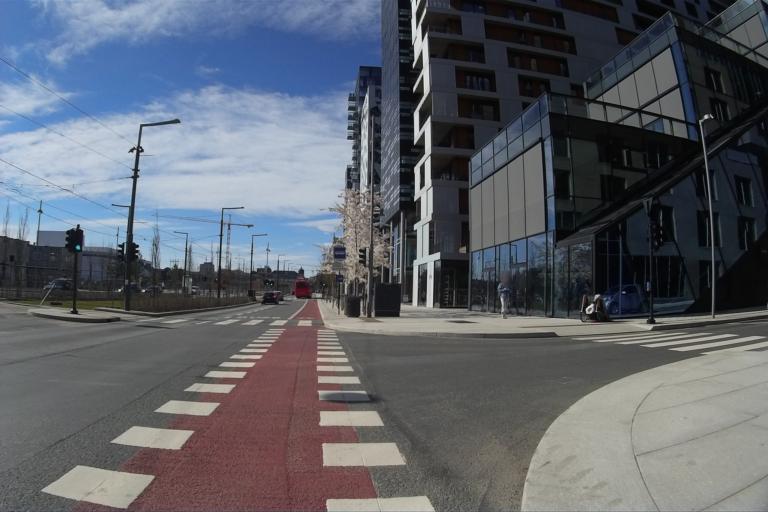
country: NO
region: Oslo
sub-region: Oslo
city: Oslo
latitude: 59.9076
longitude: 10.7597
